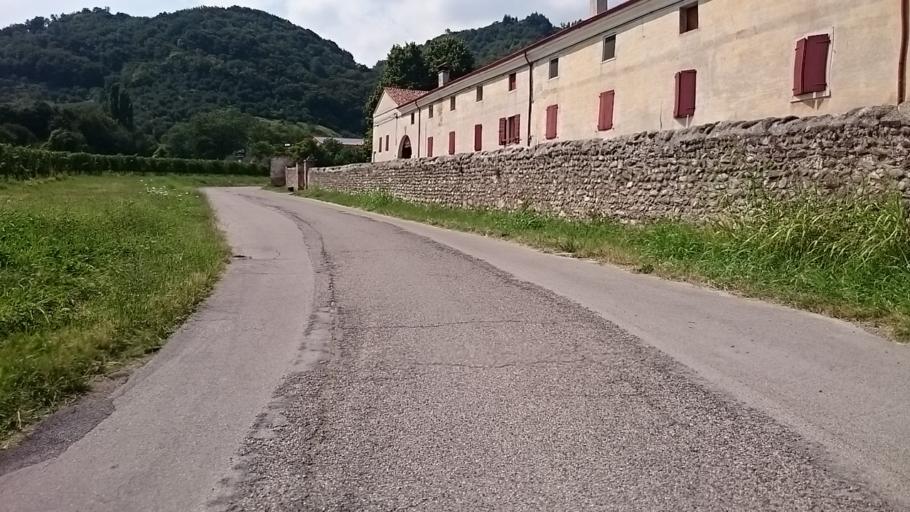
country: IT
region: Veneto
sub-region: Provincia di Vicenza
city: Pove del Grappa
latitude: 45.7803
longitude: 11.7229
